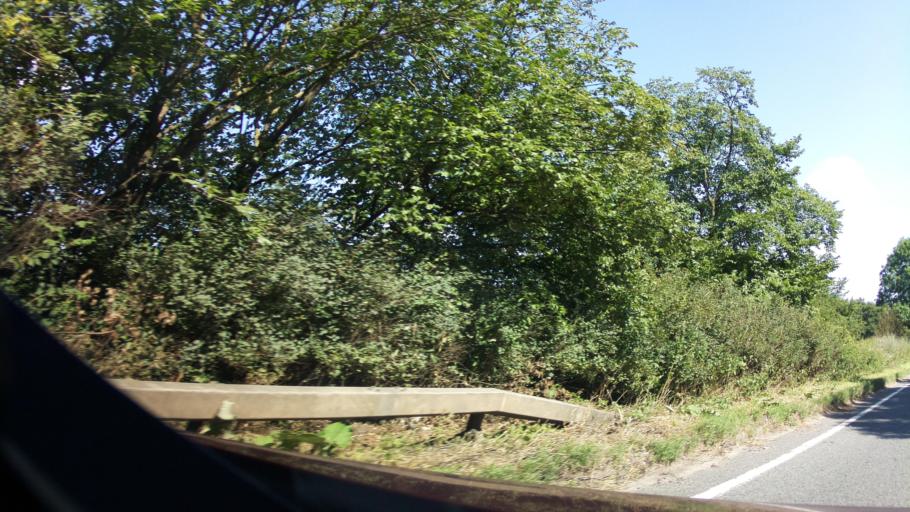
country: GB
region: England
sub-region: Warwickshire
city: Atherstone
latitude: 52.5834
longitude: -1.5669
